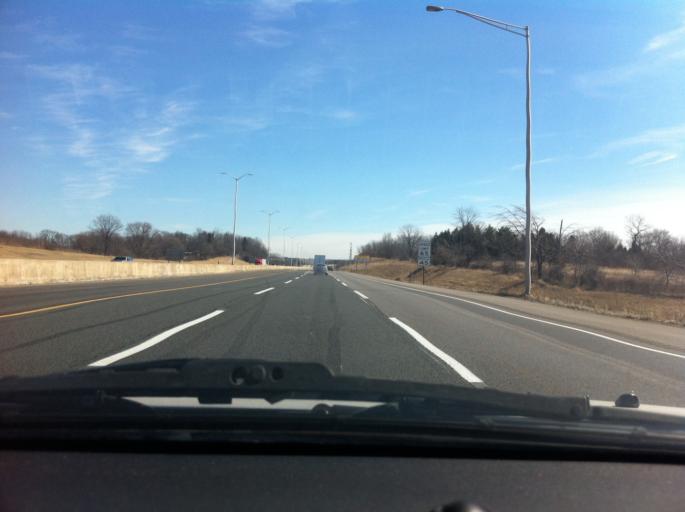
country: US
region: Illinois
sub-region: Winnebago County
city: Machesney Park
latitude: 42.3237
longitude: -88.9647
